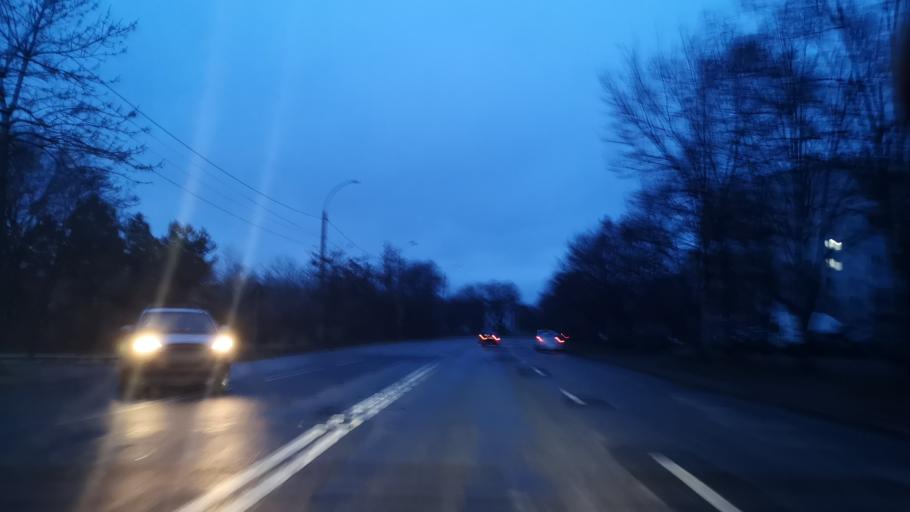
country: MD
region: Chisinau
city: Chisinau
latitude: 47.0327
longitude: 28.8785
